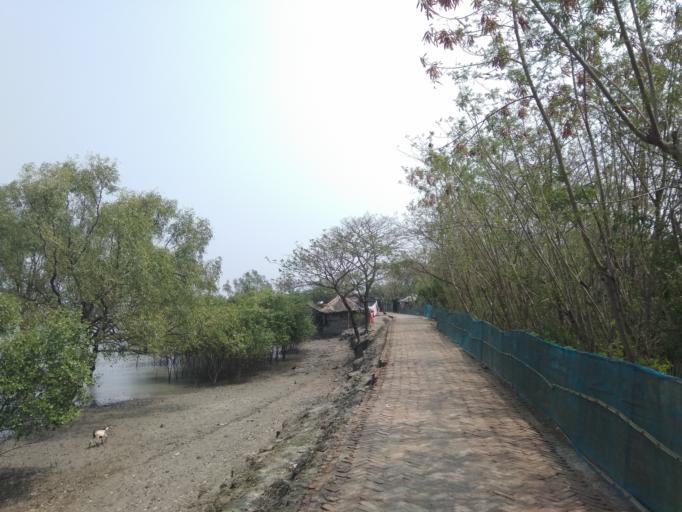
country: IN
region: West Bengal
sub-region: North 24 Parganas
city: Taki
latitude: 22.2808
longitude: 89.2895
